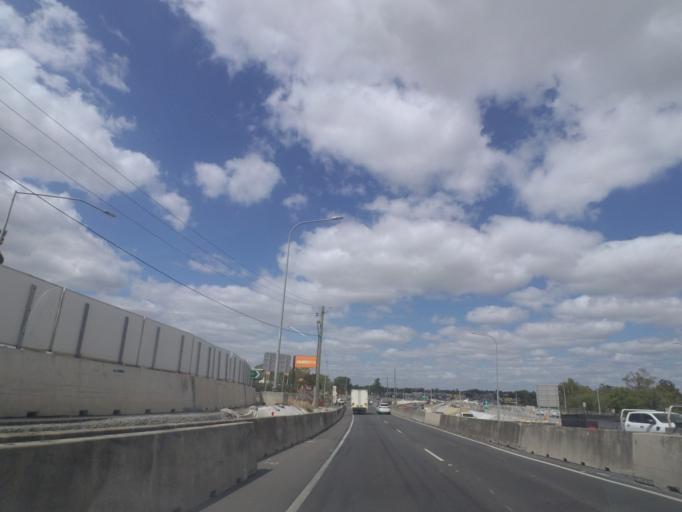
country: AU
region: Queensland
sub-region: Brisbane
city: Rocklea
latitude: -27.5635
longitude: 152.9917
